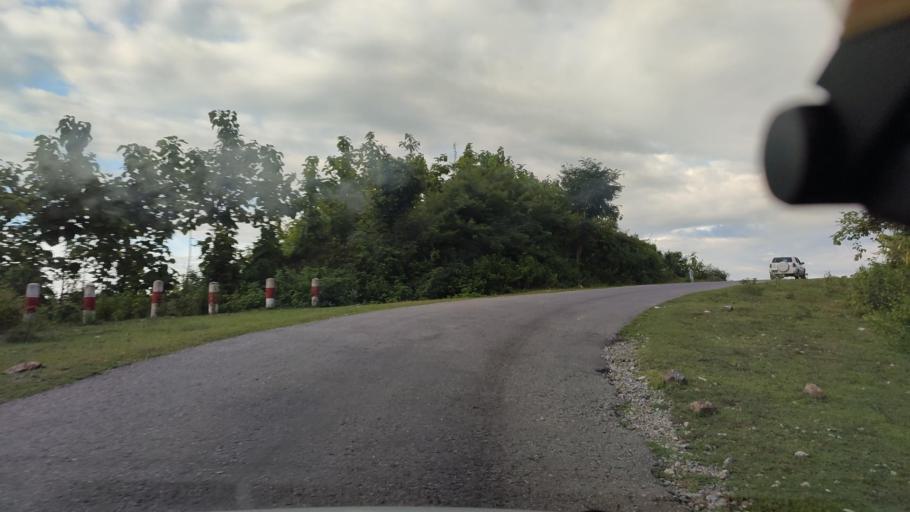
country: MM
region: Mandalay
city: Nay Pyi Taw
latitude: 19.9912
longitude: 95.8971
